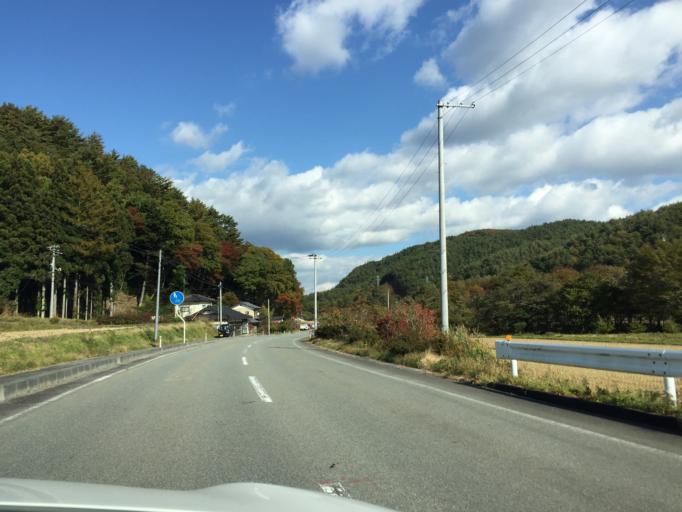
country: JP
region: Fukushima
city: Funehikimachi-funehiki
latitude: 37.3072
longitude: 140.7687
